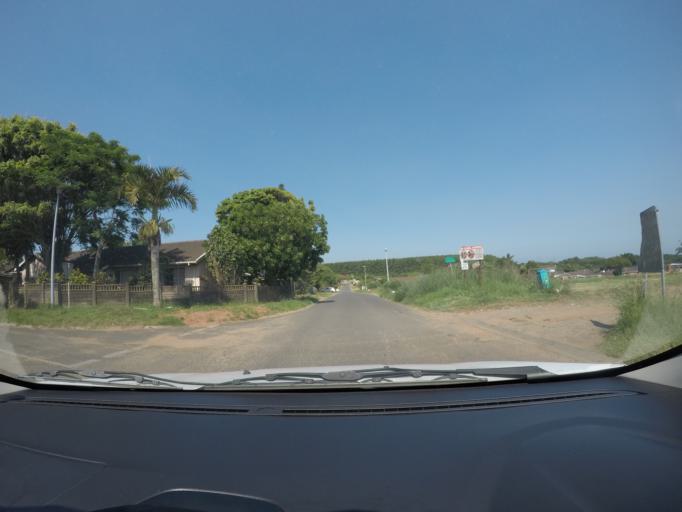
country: ZA
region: KwaZulu-Natal
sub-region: uThungulu District Municipality
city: Richards Bay
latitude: -28.7246
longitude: 32.0448
